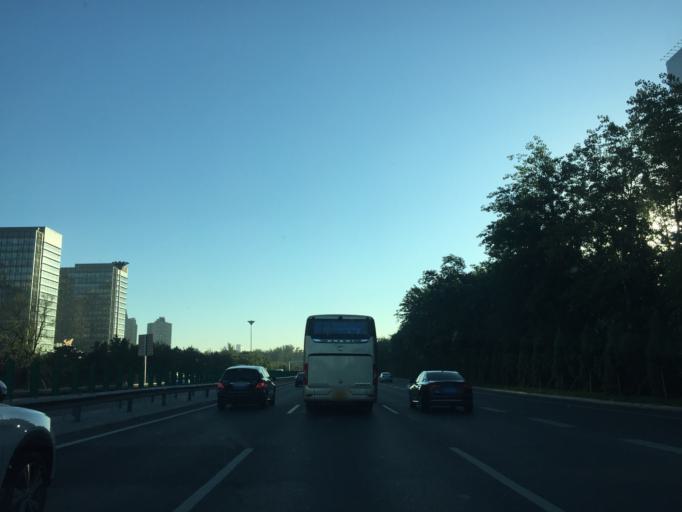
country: CN
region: Beijing
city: Wangjing
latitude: 39.9578
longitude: 116.4499
